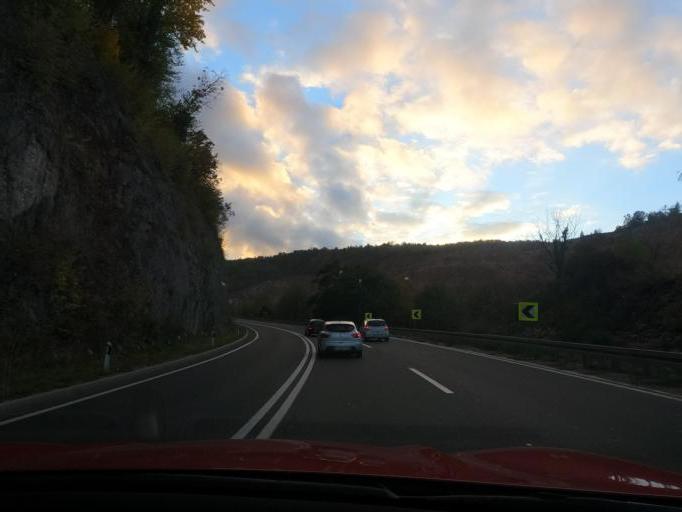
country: RS
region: Central Serbia
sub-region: Zlatiborski Okrug
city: Uzice
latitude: 43.8428
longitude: 19.8114
